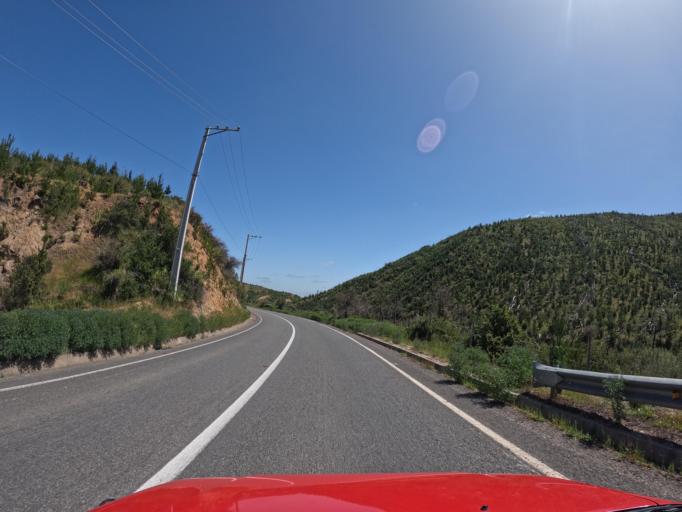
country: CL
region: O'Higgins
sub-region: Provincia de Colchagua
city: Santa Cruz
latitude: -34.6718
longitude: -71.8149
